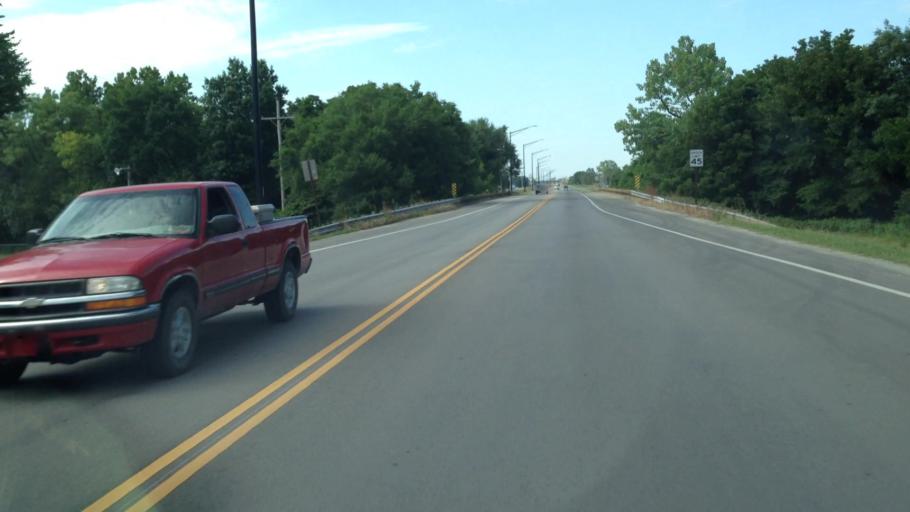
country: US
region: Kansas
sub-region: Labette County
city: Parsons
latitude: 37.3501
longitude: -95.2591
